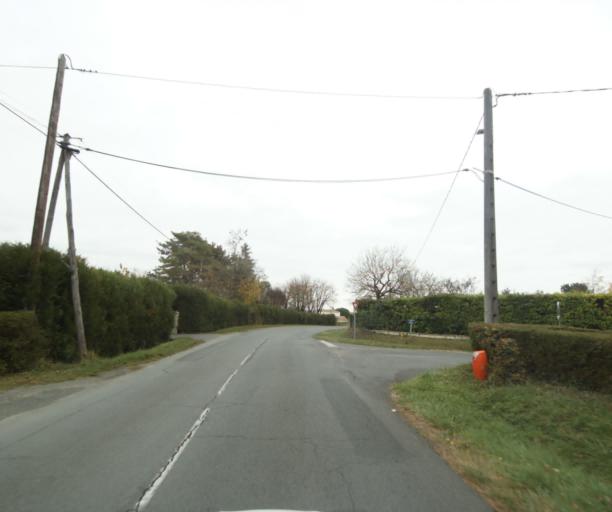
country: FR
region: Poitou-Charentes
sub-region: Departement de la Charente-Maritime
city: Les Gonds
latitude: 45.7226
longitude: -0.6343
